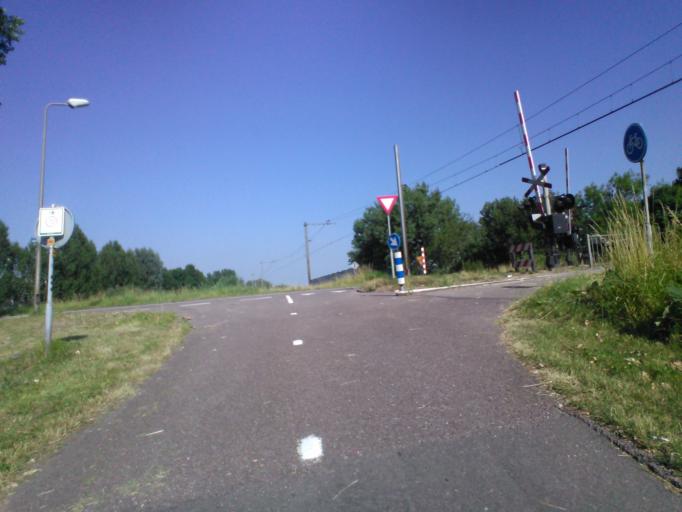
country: NL
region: South Holland
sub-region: Gemeente Alphen aan den Rijn
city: Alphen aan den Rijn
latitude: 52.1145
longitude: 4.6719
